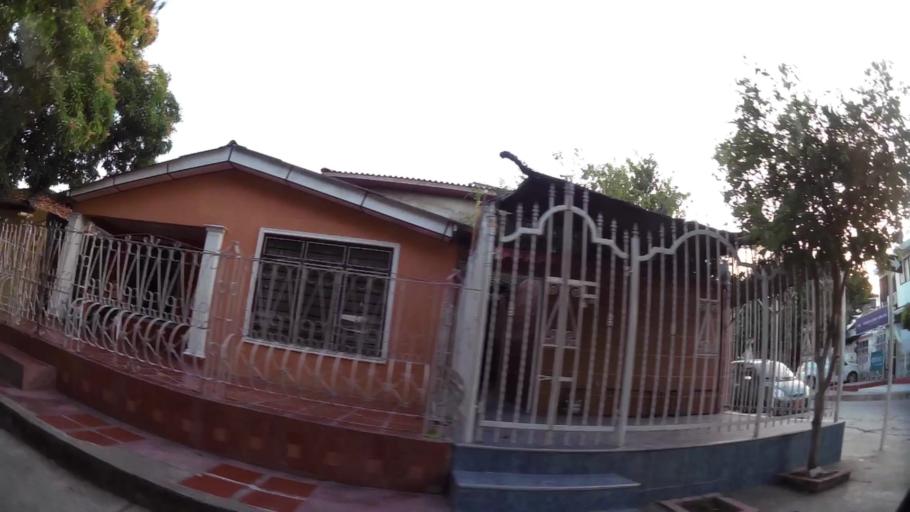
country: CO
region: Bolivar
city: Cartagena
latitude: 10.3871
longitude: -75.4896
